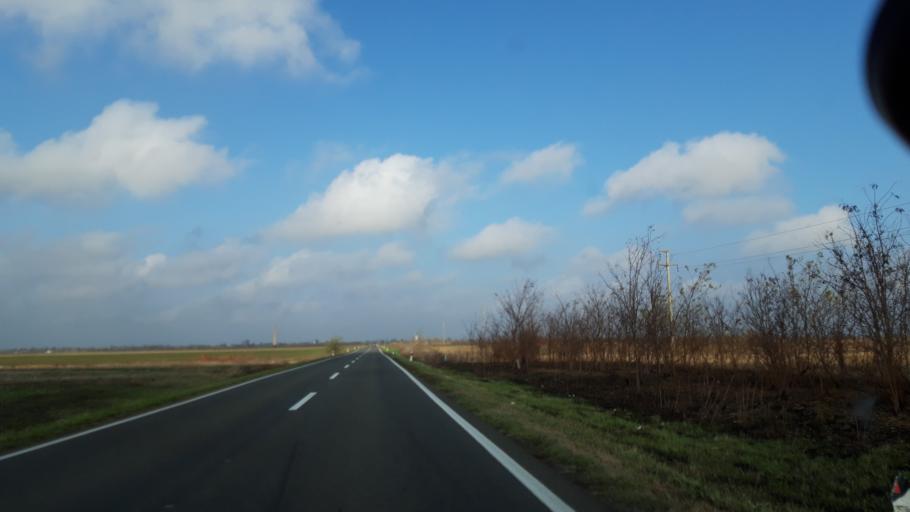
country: RS
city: Ostojicevo
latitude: 45.8716
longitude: 20.1650
